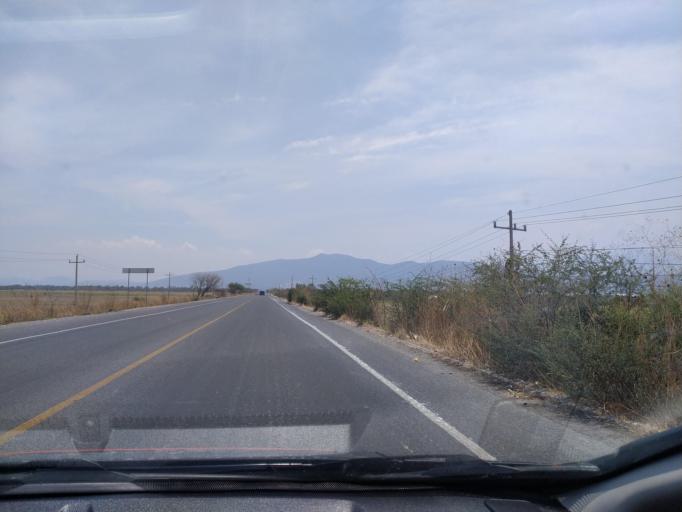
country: MX
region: Jalisco
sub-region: Zacoalco de Torres
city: Barranca de Otates (Barranca de Otatan)
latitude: 20.2986
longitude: -103.6002
